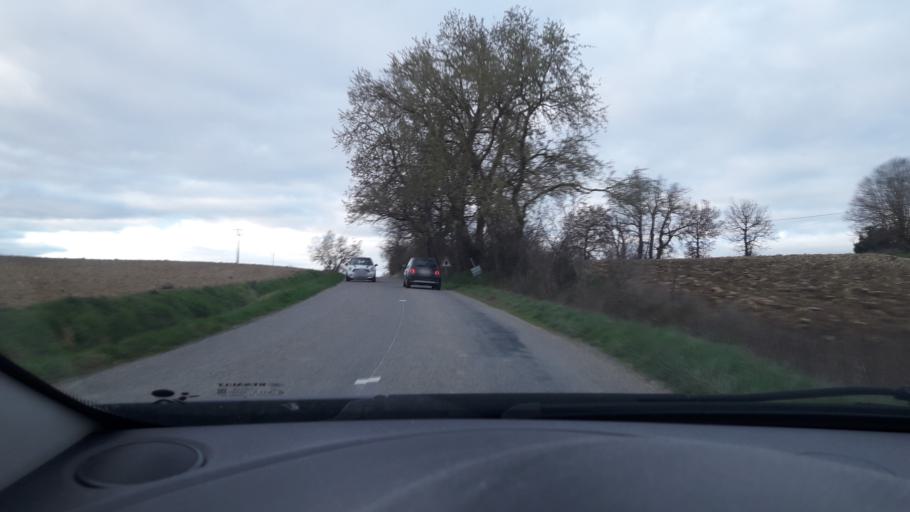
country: FR
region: Midi-Pyrenees
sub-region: Departement du Gers
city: Pujaudran
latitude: 43.6791
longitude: 1.0390
